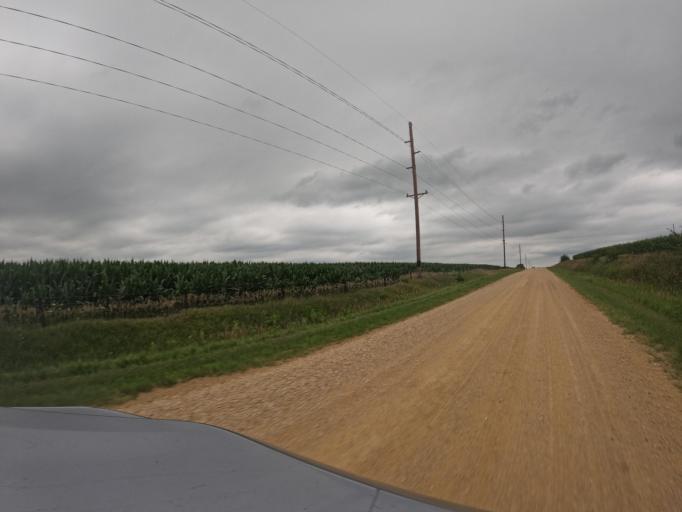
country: US
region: Iowa
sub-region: Clinton County
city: De Witt
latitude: 41.9516
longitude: -90.5870
